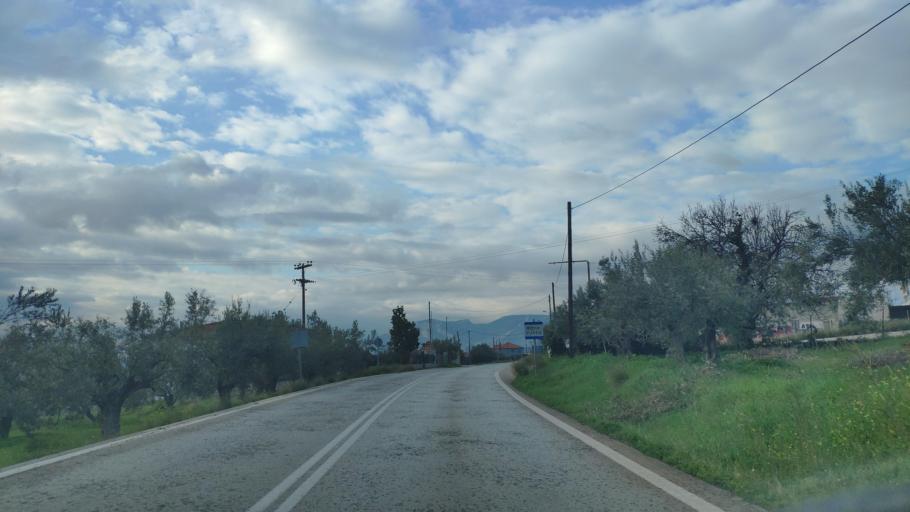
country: GR
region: Peloponnese
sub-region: Nomos Argolidos
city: Koutsopodi
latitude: 37.7280
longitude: 22.7292
